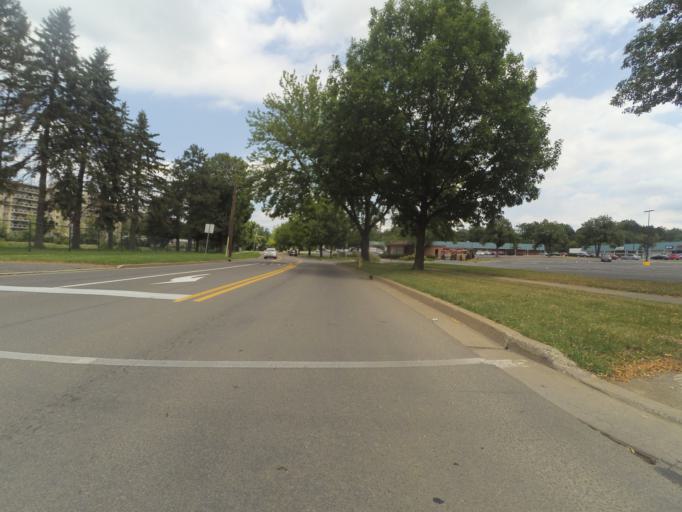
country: US
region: Pennsylvania
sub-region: Centre County
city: State College
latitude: 40.7830
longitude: -77.8537
